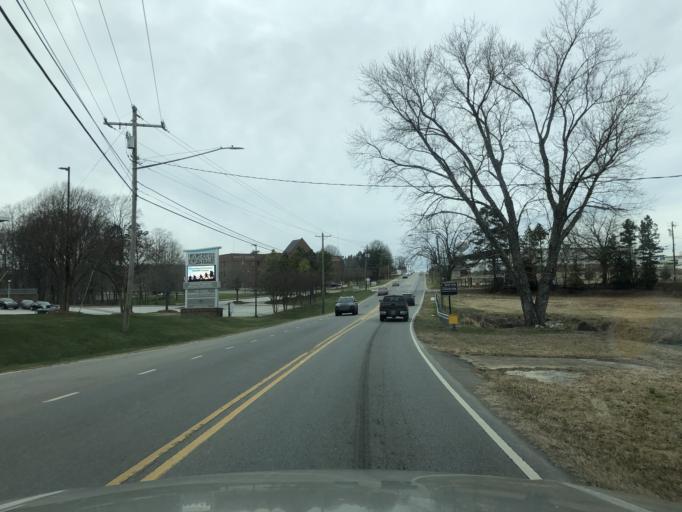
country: US
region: North Carolina
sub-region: Cleveland County
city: Shelby
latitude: 35.2778
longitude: -81.4880
